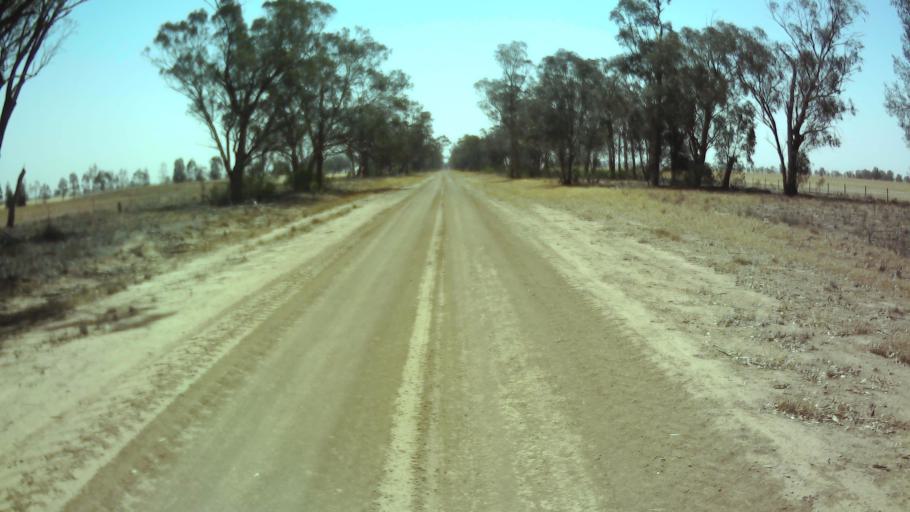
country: AU
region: New South Wales
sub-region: Weddin
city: Grenfell
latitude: -33.9312
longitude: 147.7984
